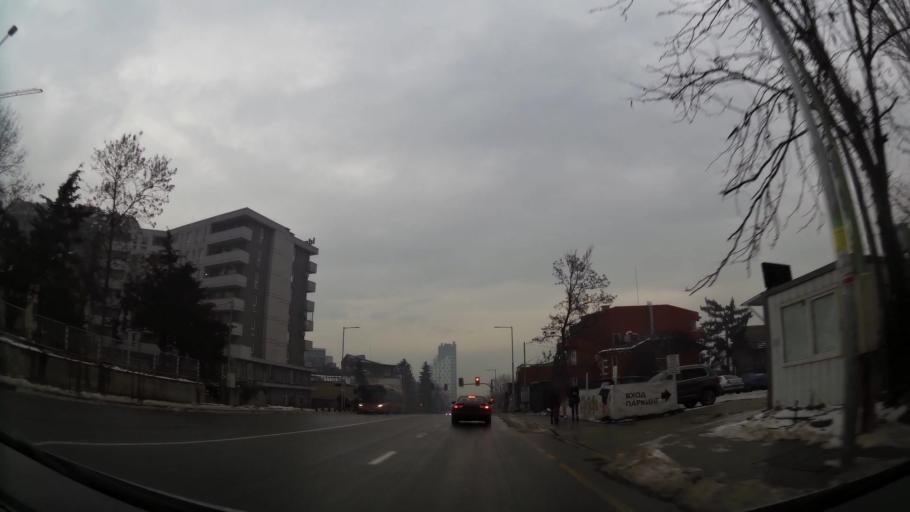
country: BG
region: Sofia-Capital
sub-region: Stolichna Obshtina
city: Sofia
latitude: 42.6762
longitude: 23.2532
